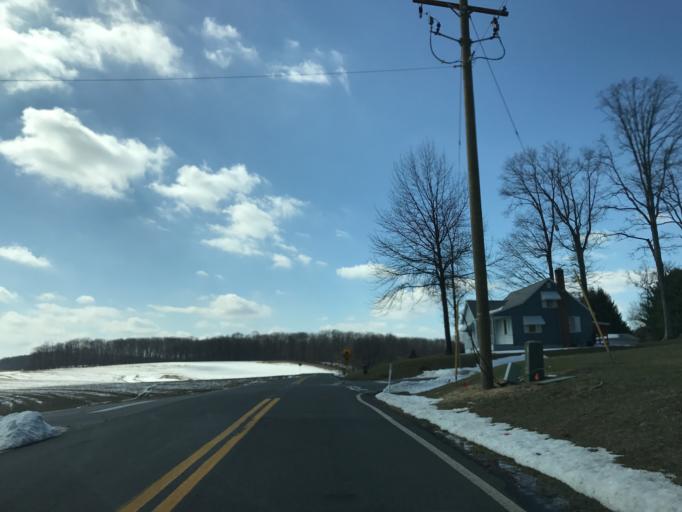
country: US
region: Maryland
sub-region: Carroll County
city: Manchester
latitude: 39.6789
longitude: -76.8237
